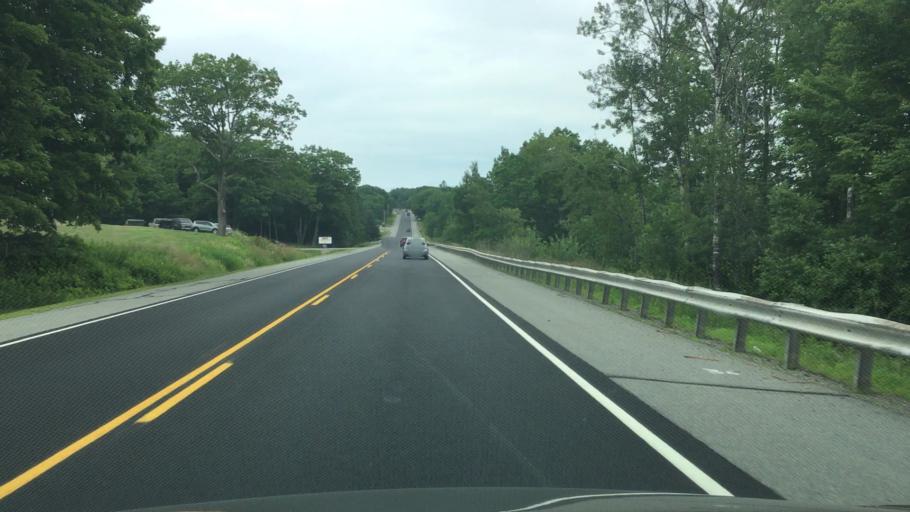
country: US
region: Maine
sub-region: Waldo County
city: Stockton Springs
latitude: 44.5032
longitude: -68.8240
